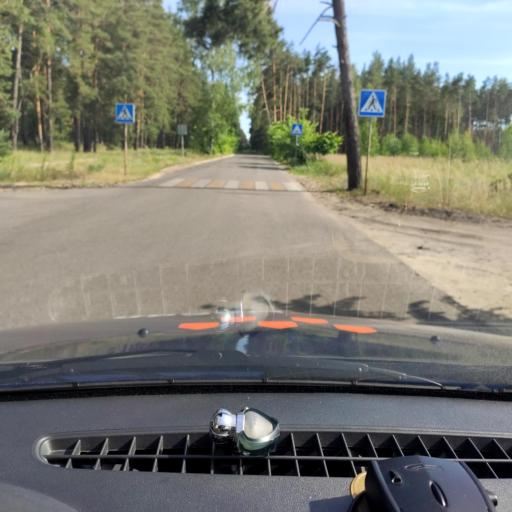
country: RU
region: Voronezj
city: Somovo
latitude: 51.7607
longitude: 39.3656
